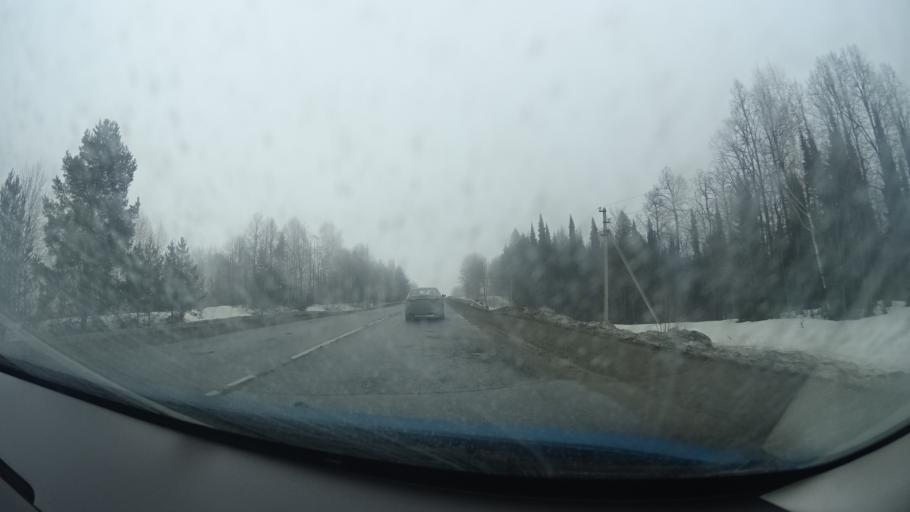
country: RU
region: Perm
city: Kuyeda
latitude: 56.4704
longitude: 55.6892
